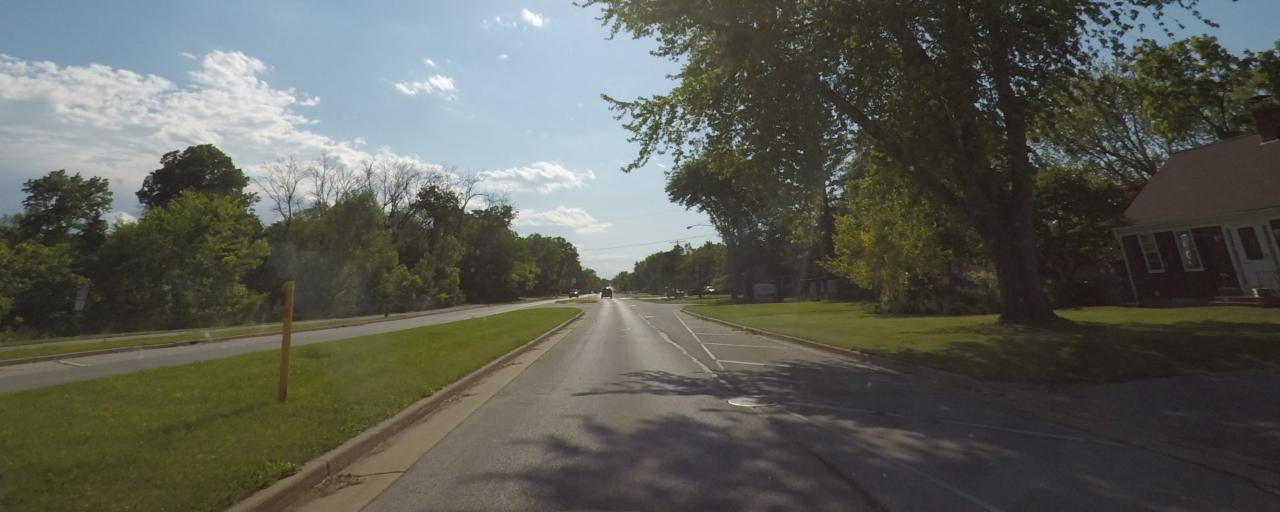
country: US
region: Wisconsin
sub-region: Milwaukee County
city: Hales Corners
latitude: 42.9447
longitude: -88.0523
